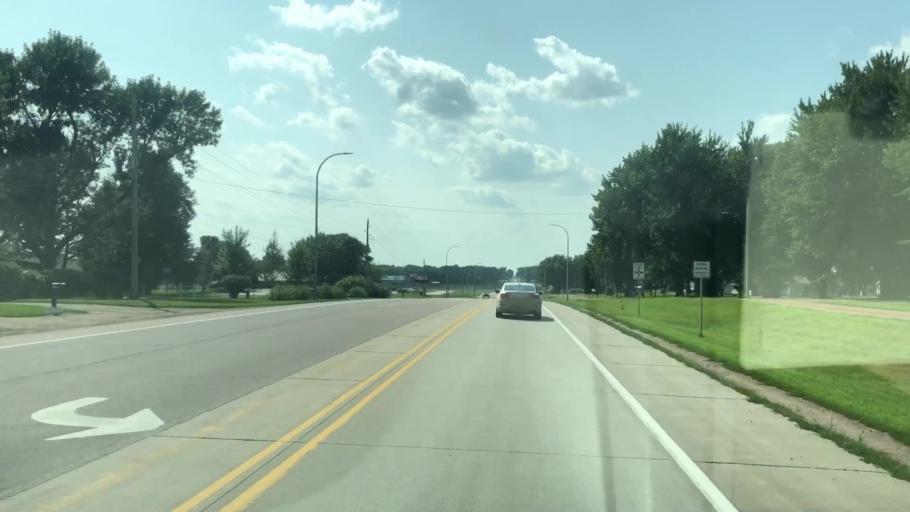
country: US
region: Iowa
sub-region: O'Brien County
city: Sheldon
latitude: 43.1861
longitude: -95.8228
